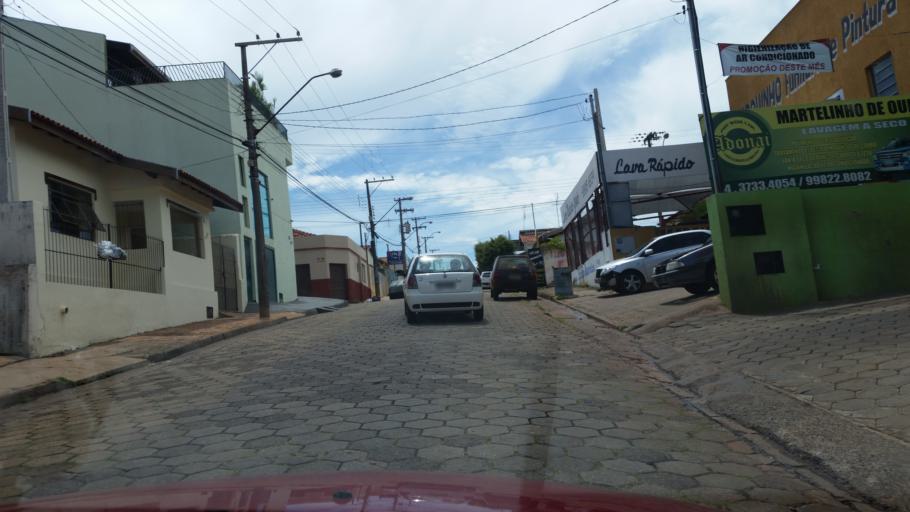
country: BR
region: Sao Paulo
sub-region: Avare
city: Avare
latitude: -23.1047
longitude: -48.9325
